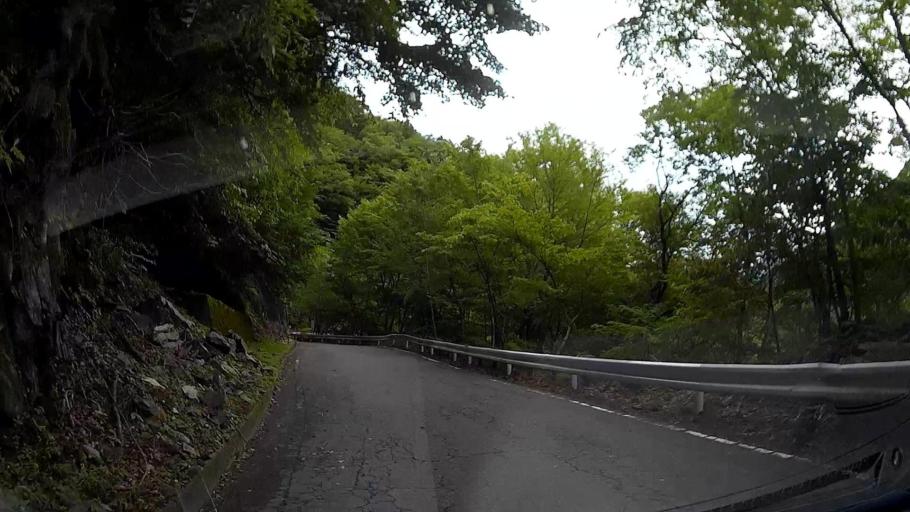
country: JP
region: Shizuoka
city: Shizuoka-shi
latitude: 35.3167
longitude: 138.1835
